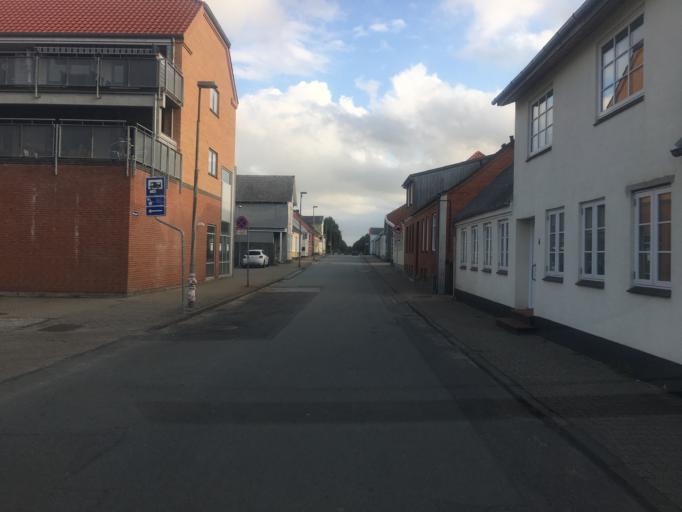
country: DK
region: South Denmark
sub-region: Tonder Kommune
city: Logumkloster
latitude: 55.0607
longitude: 8.9490
